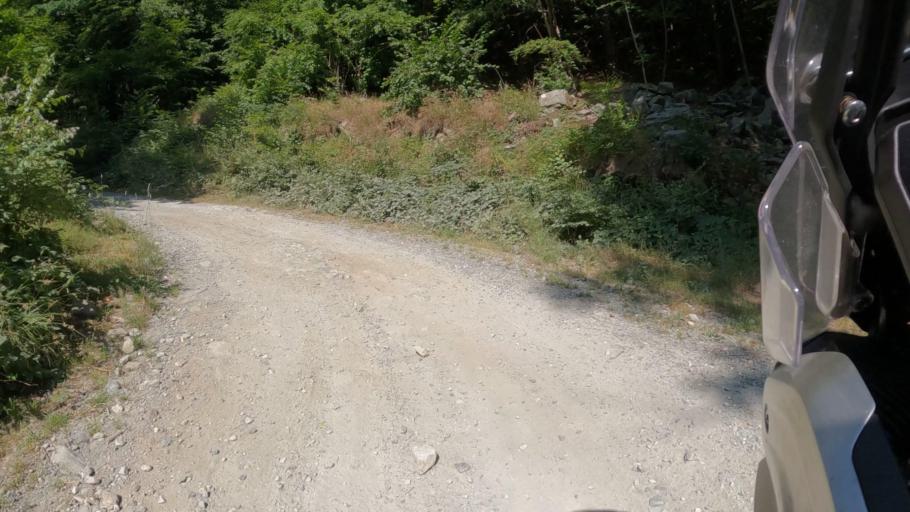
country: IT
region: Piedmont
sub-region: Provincia di Torino
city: Lemie
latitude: 45.2080
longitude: 7.3054
